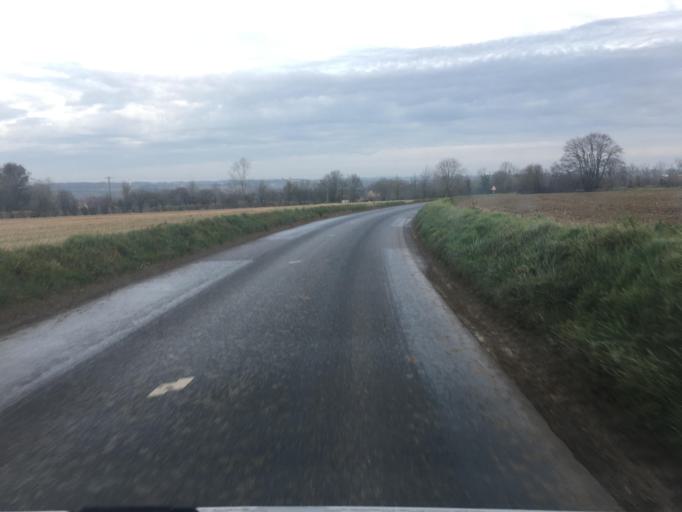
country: FR
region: Lower Normandy
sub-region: Departement du Calvados
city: Creully
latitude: 49.2669
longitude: -0.5590
